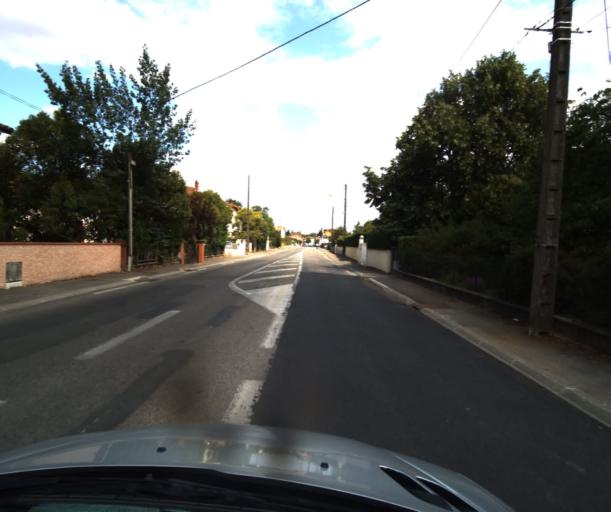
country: FR
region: Midi-Pyrenees
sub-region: Departement du Tarn-et-Garonne
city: Montauban
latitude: 44.0055
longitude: 1.3496
